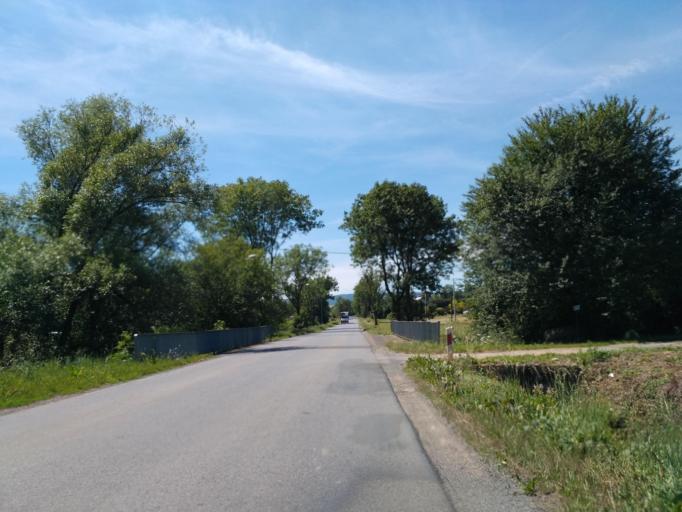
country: PL
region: Subcarpathian Voivodeship
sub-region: Powiat sanocki
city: Bukowsko
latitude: 49.5003
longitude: 22.0765
